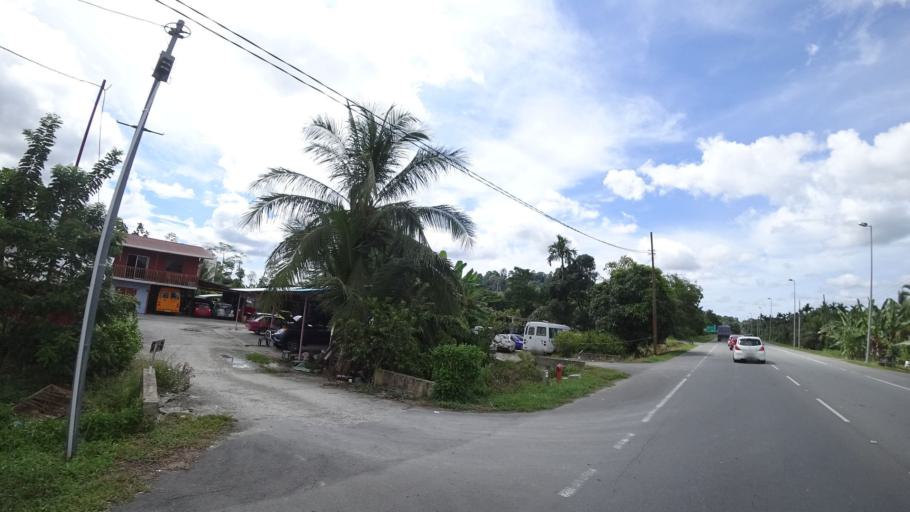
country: BN
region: Tutong
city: Tutong
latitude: 4.7465
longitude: 114.8154
